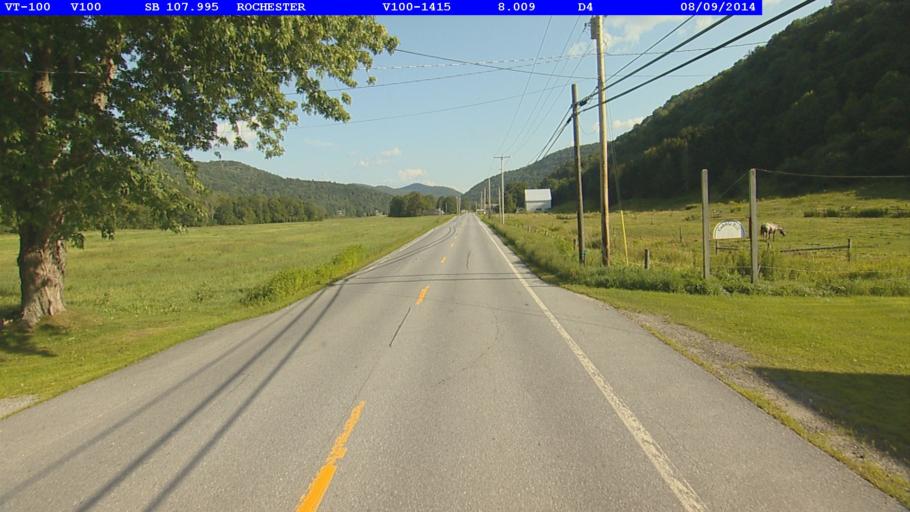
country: US
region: Vermont
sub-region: Orange County
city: Randolph
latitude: 43.9081
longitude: -72.8299
